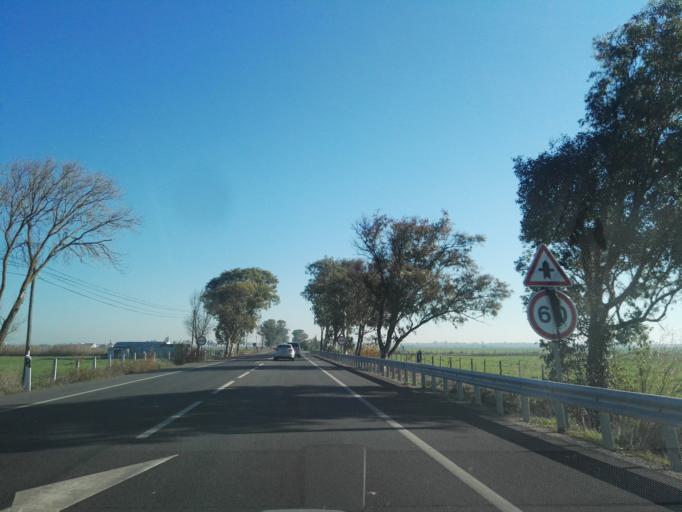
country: PT
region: Santarem
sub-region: Benavente
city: Samora Correia
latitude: 38.9336
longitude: -8.9188
